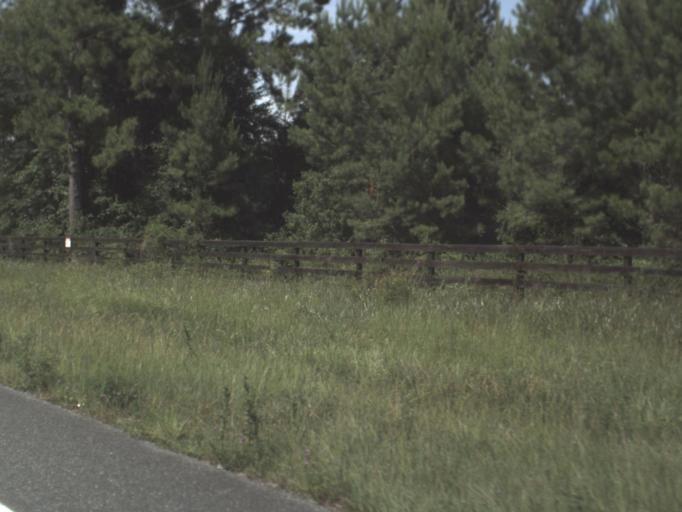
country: US
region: Florida
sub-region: Alachua County
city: High Springs
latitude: 29.8235
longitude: -82.7415
